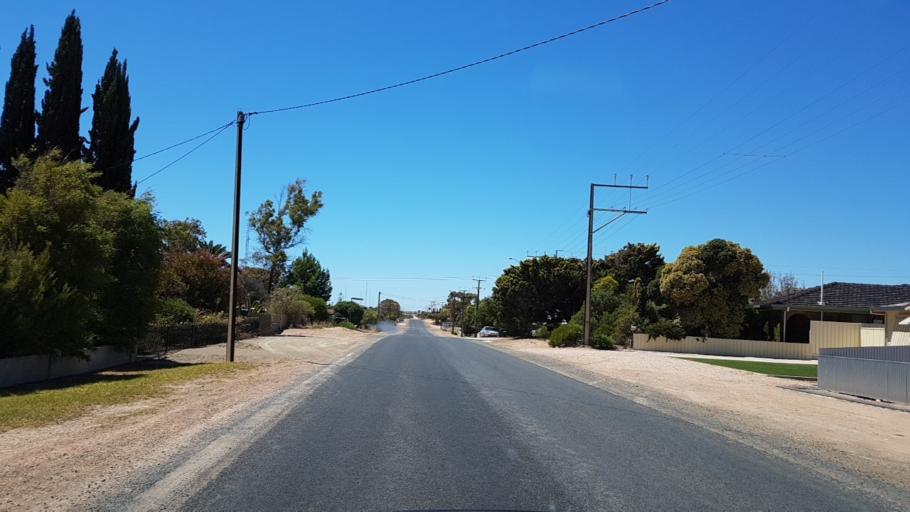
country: AU
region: South Australia
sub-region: Copper Coast
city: Wallaroo
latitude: -34.0526
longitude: 137.5666
